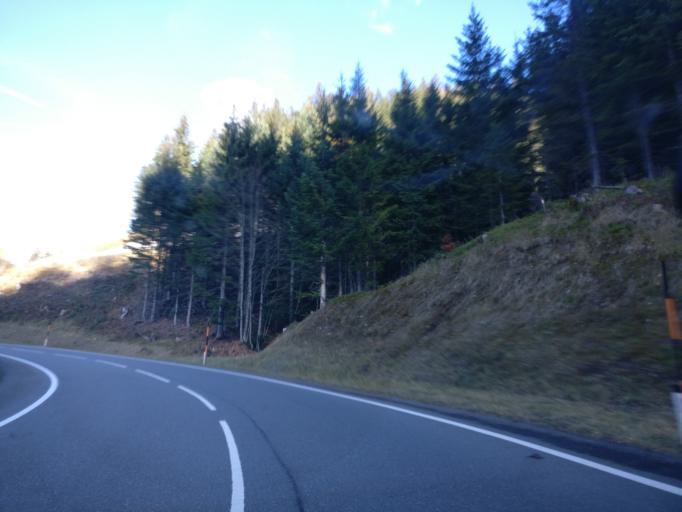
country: AT
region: Salzburg
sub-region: Politischer Bezirk Zell am See
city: Dienten am Hochkonig
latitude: 47.4025
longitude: 12.9913
